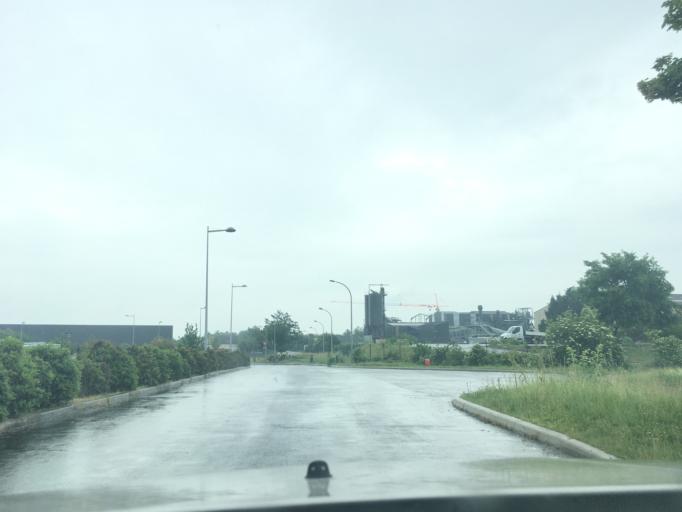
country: FR
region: Poitou-Charentes
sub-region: Departement de la Charente
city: Saint-Brice
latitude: 45.6780
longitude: -0.3026
